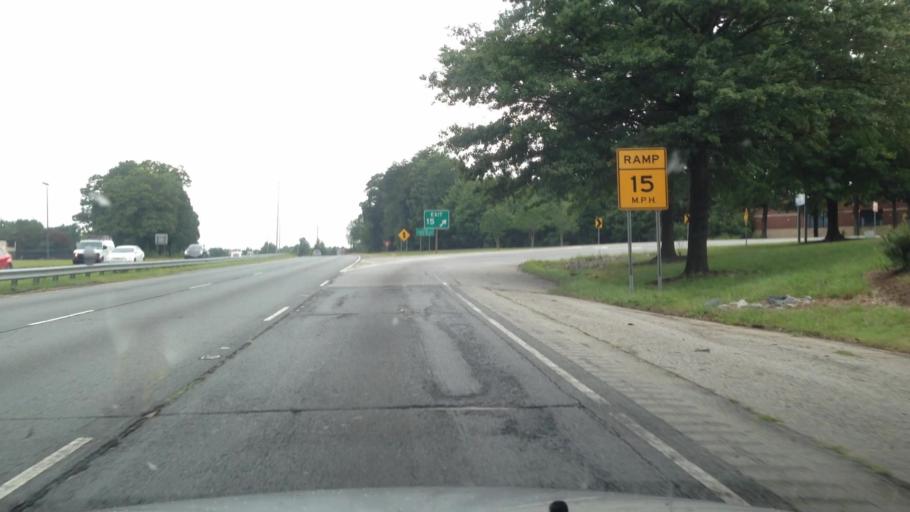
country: US
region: North Carolina
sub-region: Forsyth County
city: Kernersville
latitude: 36.1132
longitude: -80.0642
